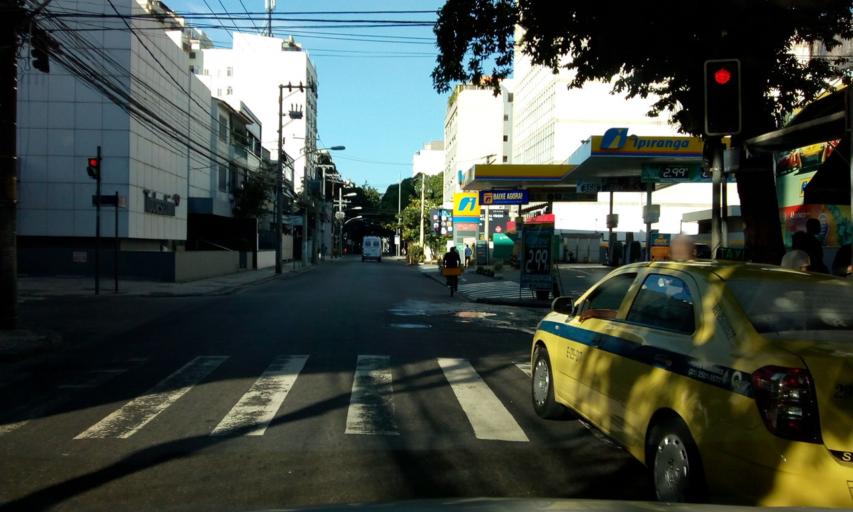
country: BR
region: Rio de Janeiro
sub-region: Rio De Janeiro
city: Rio de Janeiro
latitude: -22.9543
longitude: -43.1866
